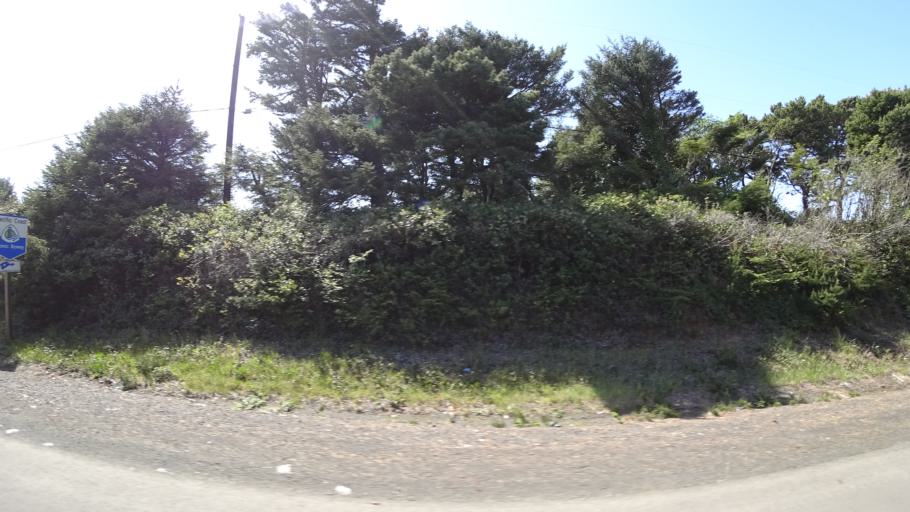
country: US
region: Oregon
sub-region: Lincoln County
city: Newport
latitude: 44.6936
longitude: -124.0629
